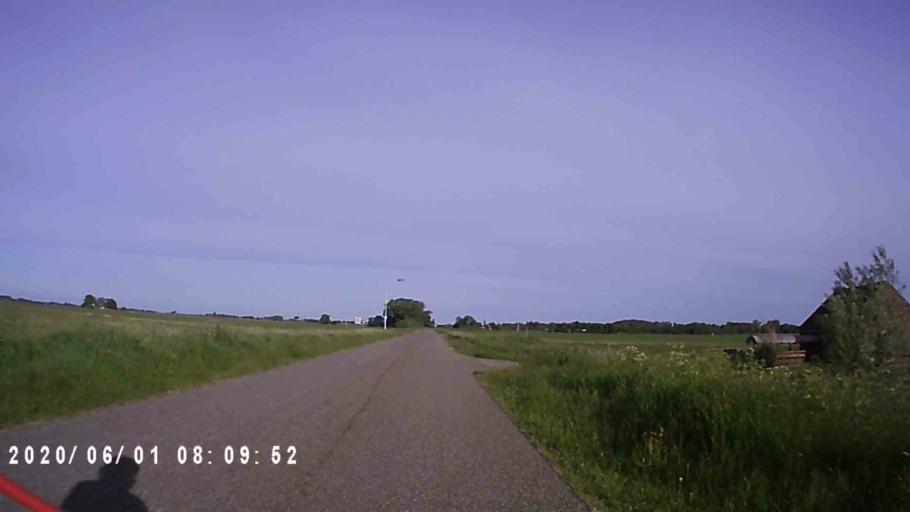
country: NL
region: Friesland
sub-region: Gemeente Ferwerderadiel
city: Burdaard
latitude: 53.2857
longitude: 5.8911
